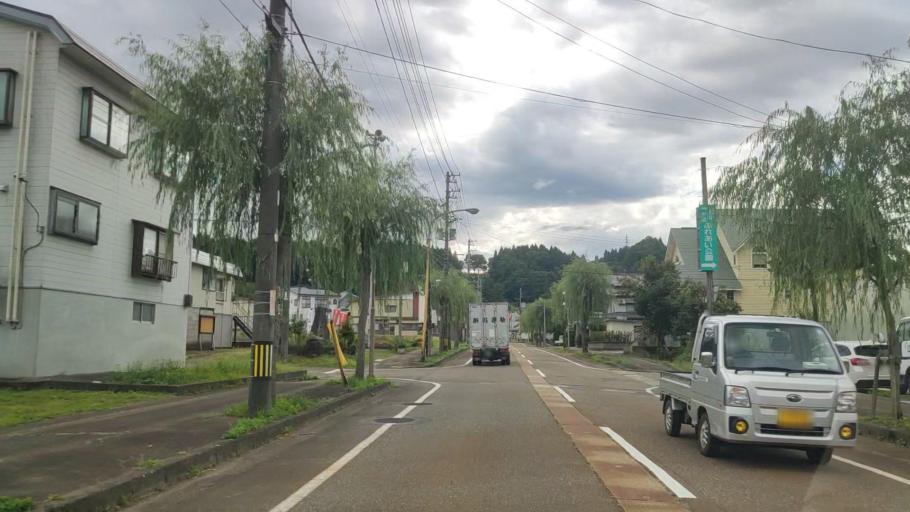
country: JP
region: Niigata
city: Arai
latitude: 37.0141
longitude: 138.2499
